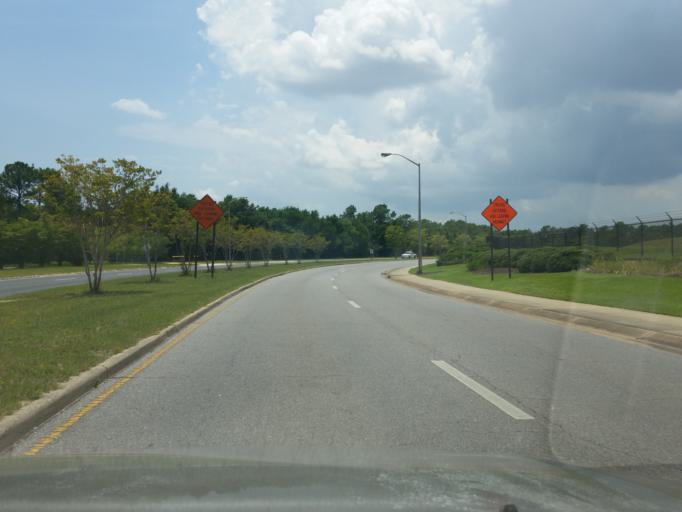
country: US
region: Florida
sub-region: Escambia County
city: East Pensacola Heights
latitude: 30.4580
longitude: -87.1823
